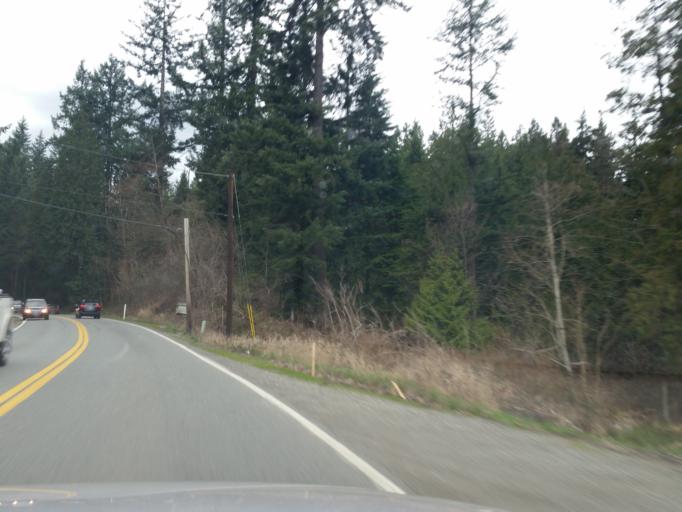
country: US
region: Washington
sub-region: Snohomish County
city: North Creek
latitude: 47.8085
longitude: -122.1647
